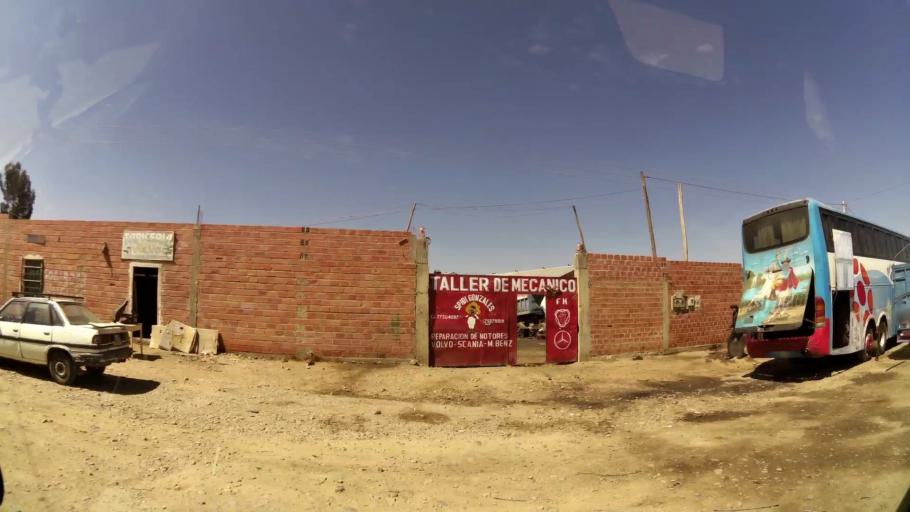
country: BO
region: La Paz
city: La Paz
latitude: -16.5511
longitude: -68.1841
